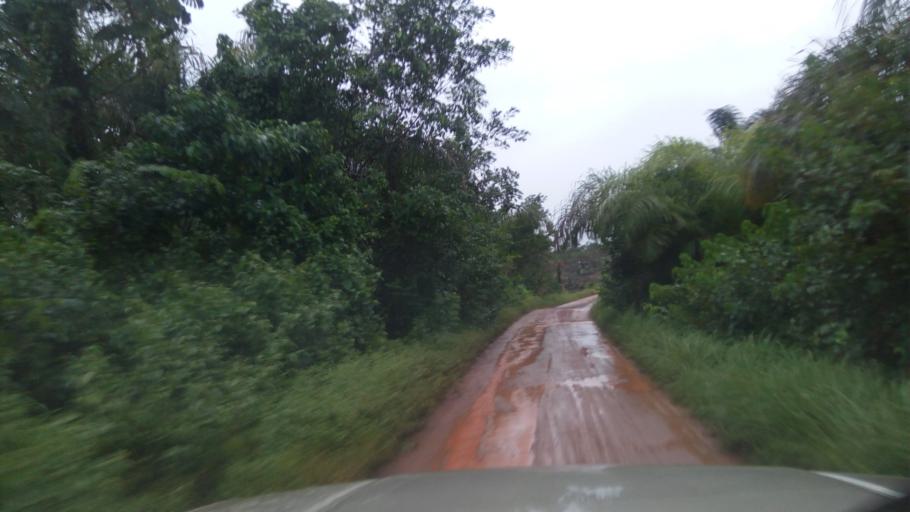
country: SL
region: Southern Province
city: Zimmi
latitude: 7.2730
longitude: -11.2509
